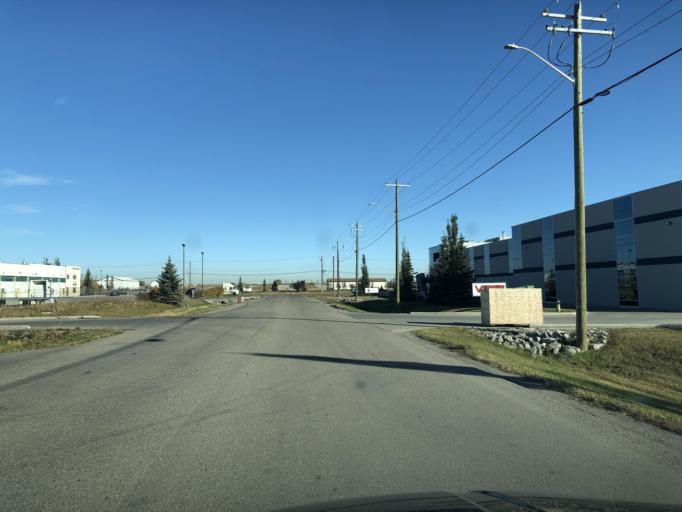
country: CA
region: Alberta
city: Chestermere
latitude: 50.9686
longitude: -113.9026
